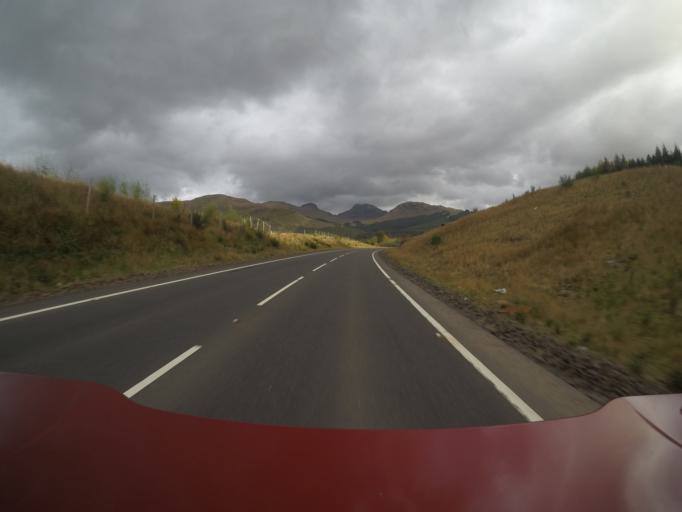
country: GB
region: Scotland
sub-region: Argyll and Bute
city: Garelochhead
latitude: 56.3920
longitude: -4.6220
